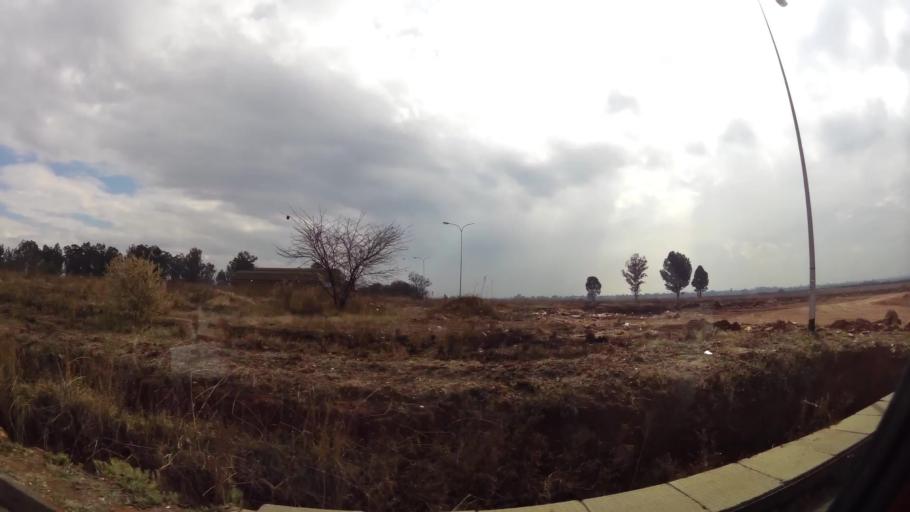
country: ZA
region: Gauteng
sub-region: Sedibeng District Municipality
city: Vanderbijlpark
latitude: -26.7261
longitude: 27.8768
